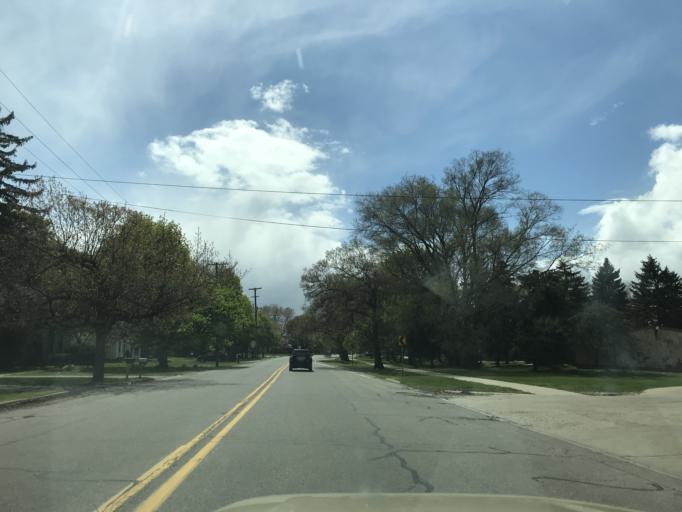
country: US
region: Michigan
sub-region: Wayne County
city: Plymouth
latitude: 42.3858
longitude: -83.4491
